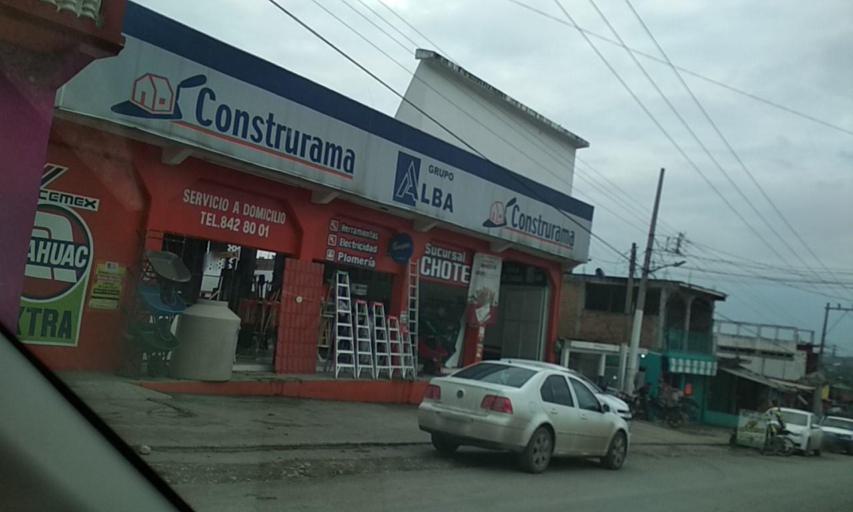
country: MX
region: Veracruz
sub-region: Papantla
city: El Chote
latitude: 20.4023
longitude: -97.3386
